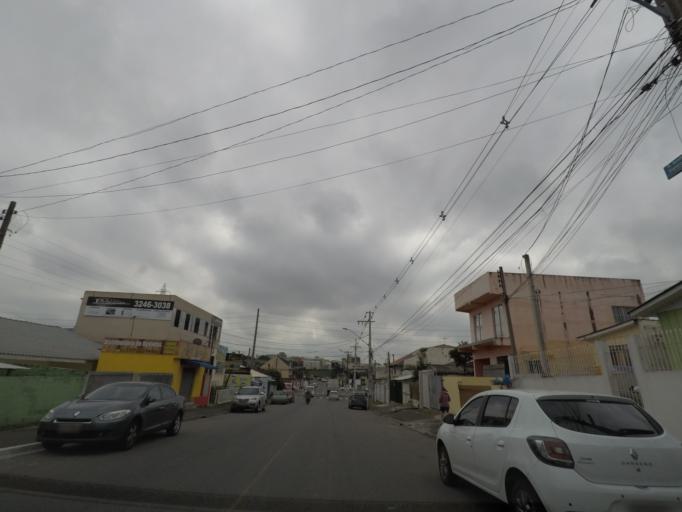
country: BR
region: Parana
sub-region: Curitiba
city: Curitiba
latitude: -25.5145
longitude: -49.3098
